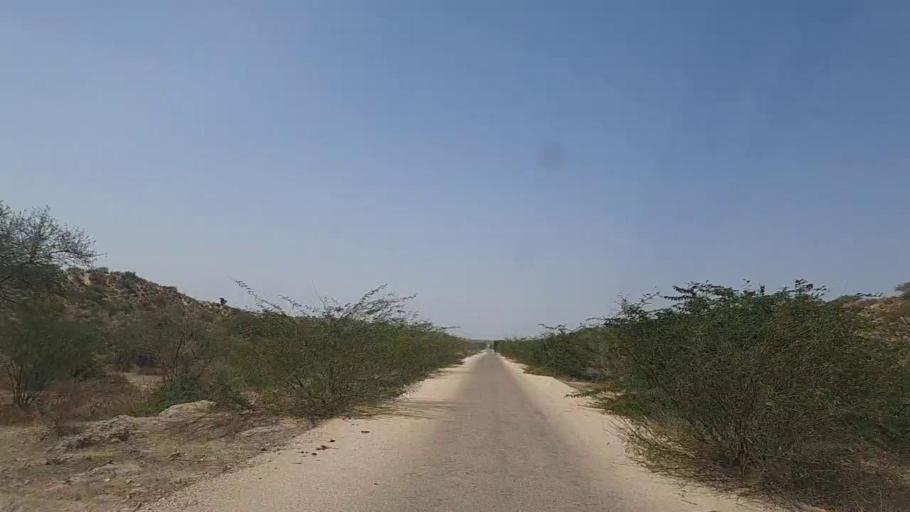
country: PK
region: Sindh
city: Diplo
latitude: 24.5186
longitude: 69.3488
